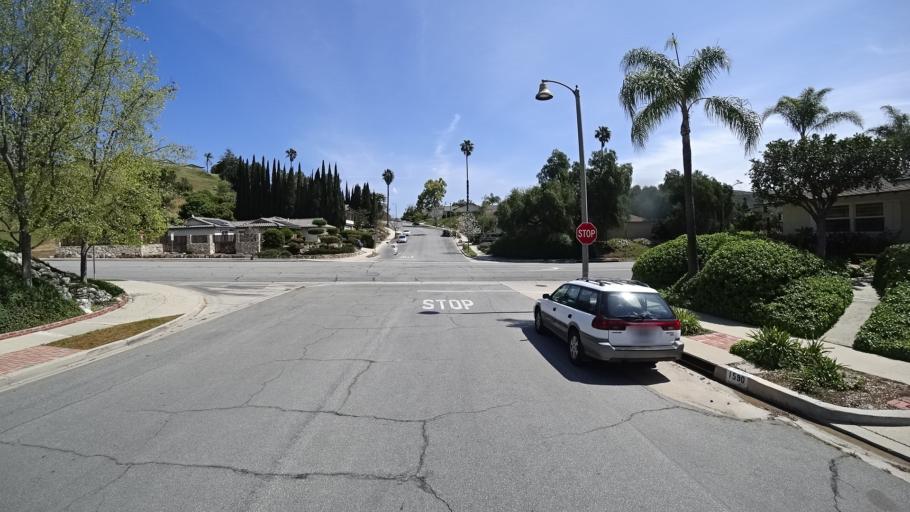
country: US
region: California
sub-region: Ventura County
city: Moorpark
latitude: 34.2389
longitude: -118.8486
